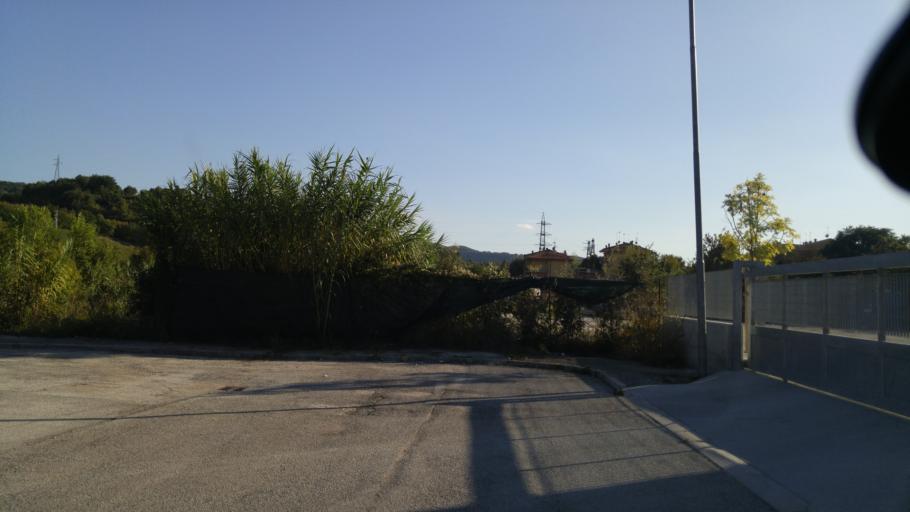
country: IT
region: The Marches
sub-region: Provincia di Pesaro e Urbino
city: Fermignano
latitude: 43.6874
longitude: 12.6494
